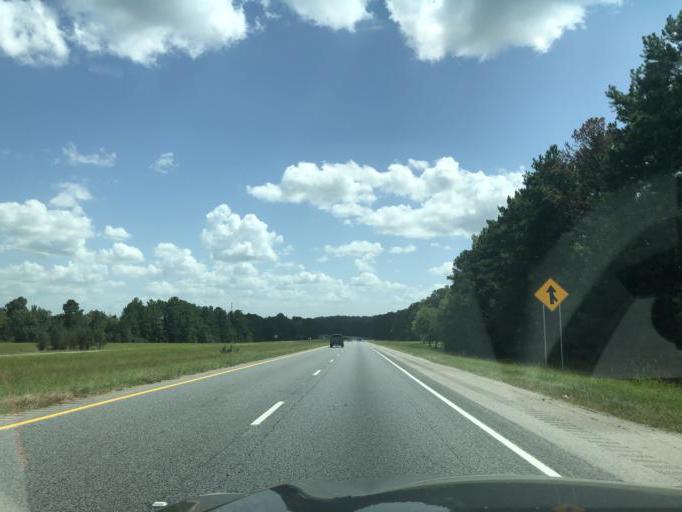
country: US
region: Georgia
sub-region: Troup County
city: La Grange
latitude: 33.0116
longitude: -84.9531
